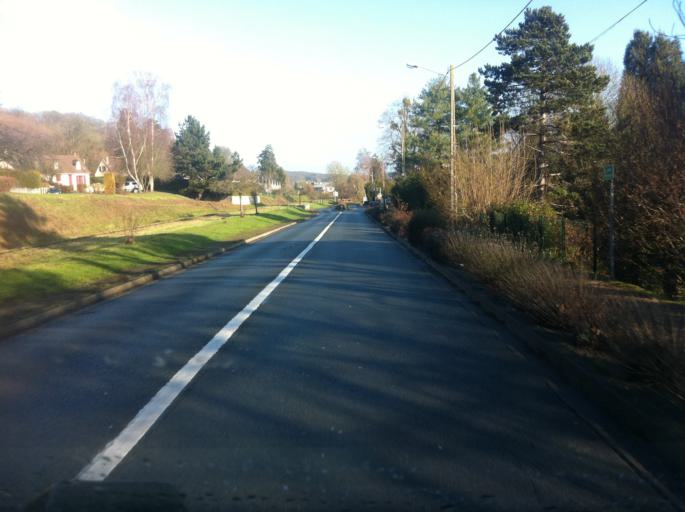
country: FR
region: Haute-Normandie
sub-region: Departement de la Seine-Maritime
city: Duclair
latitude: 49.4758
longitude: 0.8653
